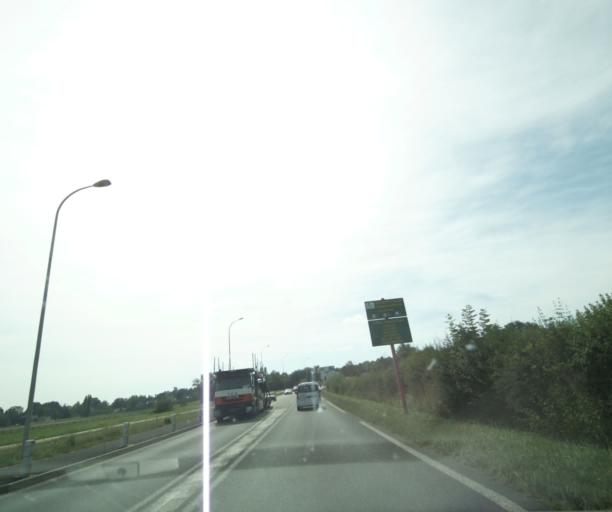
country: FR
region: Auvergne
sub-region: Departement de l'Allier
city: Bellerive-sur-Allier
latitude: 46.1295
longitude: 3.4017
